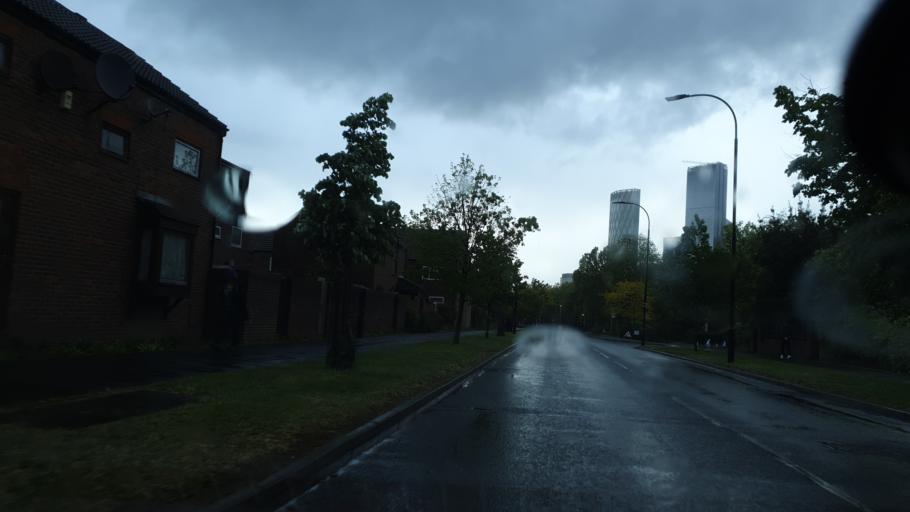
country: GB
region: England
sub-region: Greater London
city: Poplar
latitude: 51.4974
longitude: -0.0380
